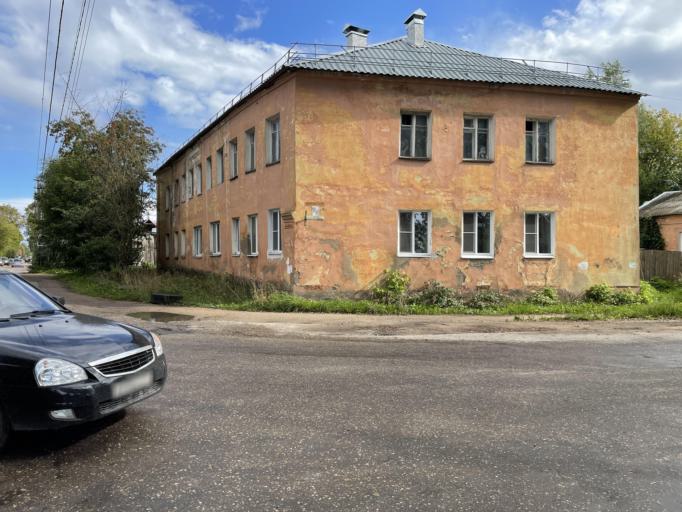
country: RU
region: Tverskaya
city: Vyshniy Volochek
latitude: 57.5801
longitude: 34.5585
